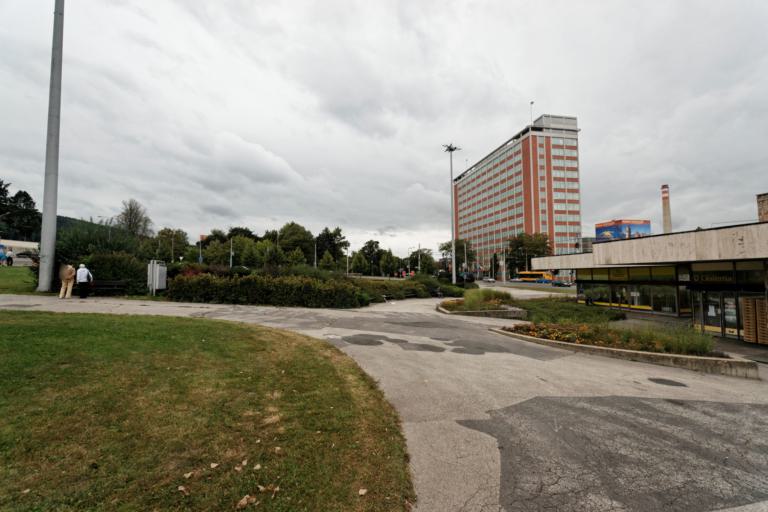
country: CZ
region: Zlin
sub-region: Okres Zlin
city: Zlin
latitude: 49.2228
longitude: 17.6609
